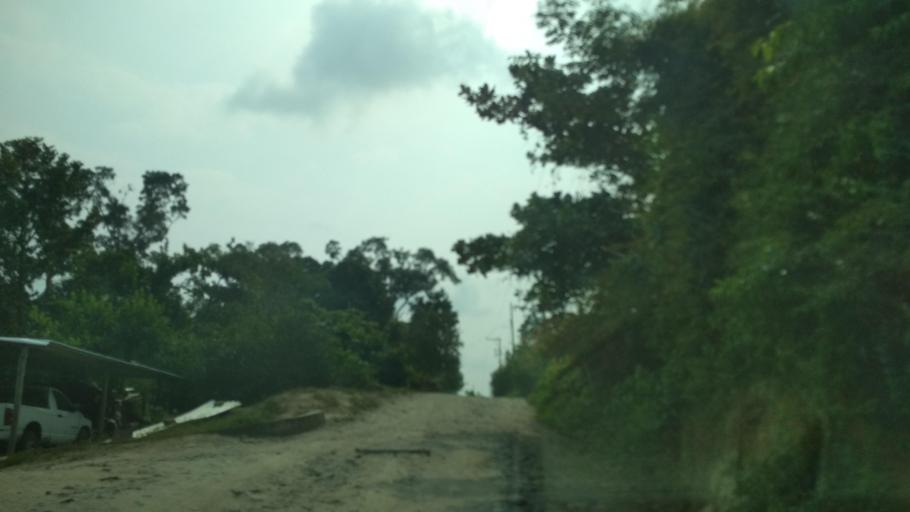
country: MM
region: Kayah
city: Loikaw
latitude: 20.2163
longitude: 97.2849
